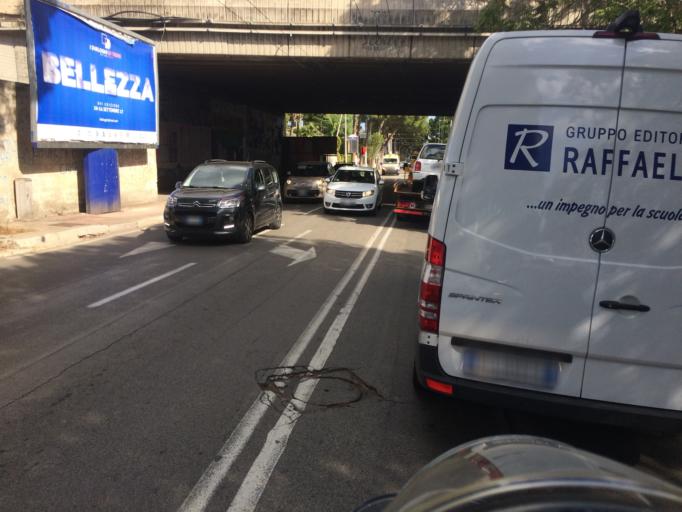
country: IT
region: Apulia
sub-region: Provincia di Bari
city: Bari
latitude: 41.0893
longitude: 16.8696
